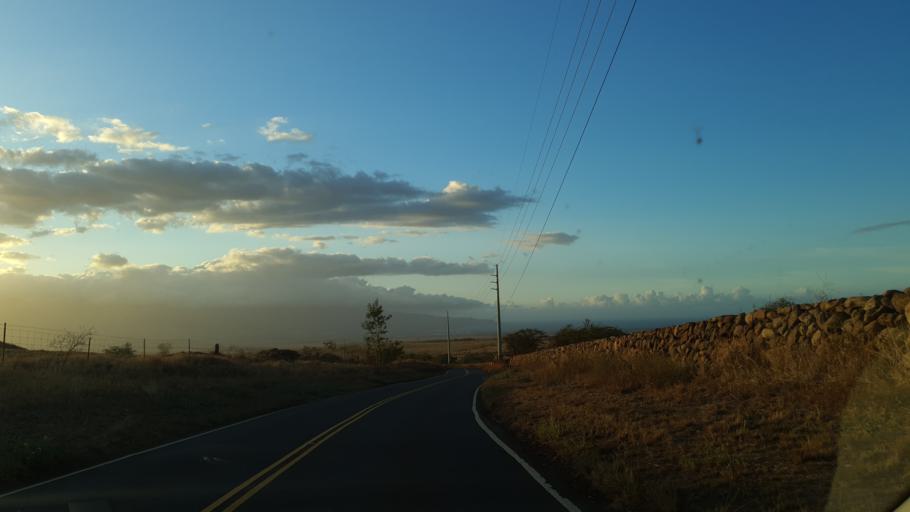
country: US
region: Hawaii
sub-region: Maui County
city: Pukalani
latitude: 20.8006
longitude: -156.3742
